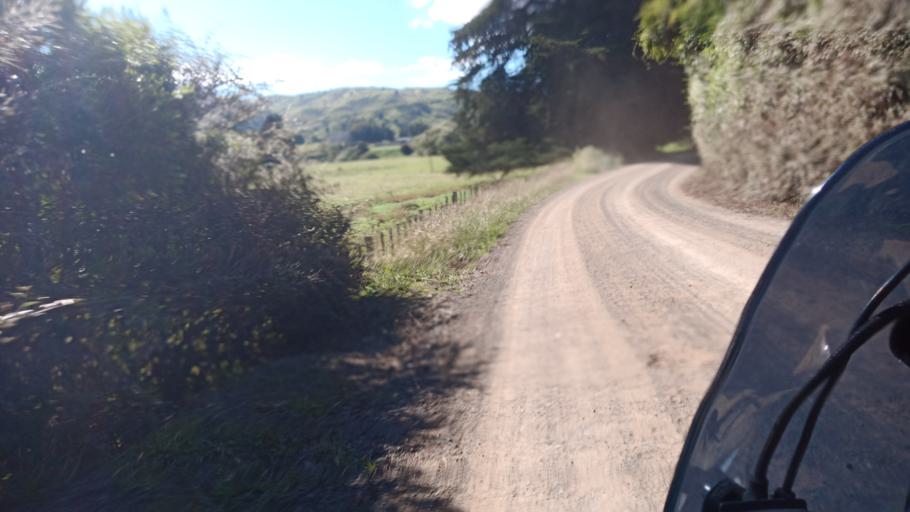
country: NZ
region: Bay of Plenty
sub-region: Opotiki District
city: Opotiki
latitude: -38.2554
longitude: 177.5738
